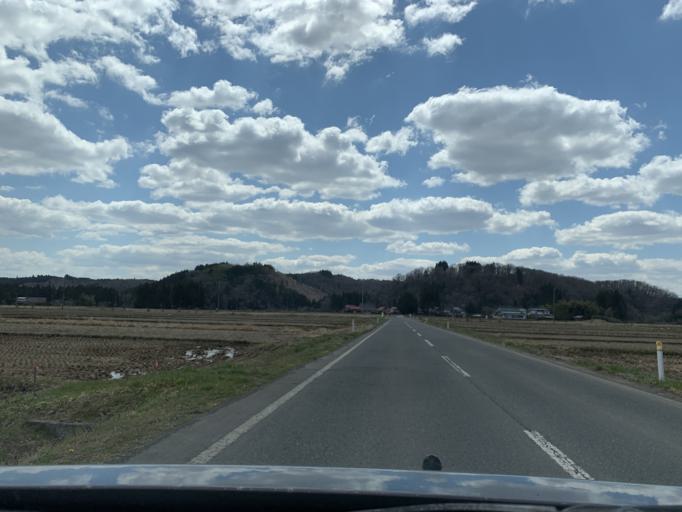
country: JP
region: Iwate
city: Ichinoseki
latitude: 38.9253
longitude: 141.0820
